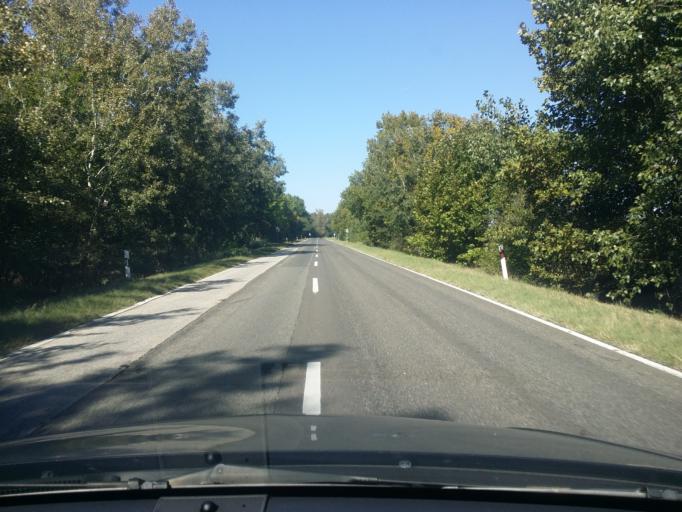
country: HU
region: Bacs-Kiskun
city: Palmonostora
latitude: 46.5849
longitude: 19.9266
